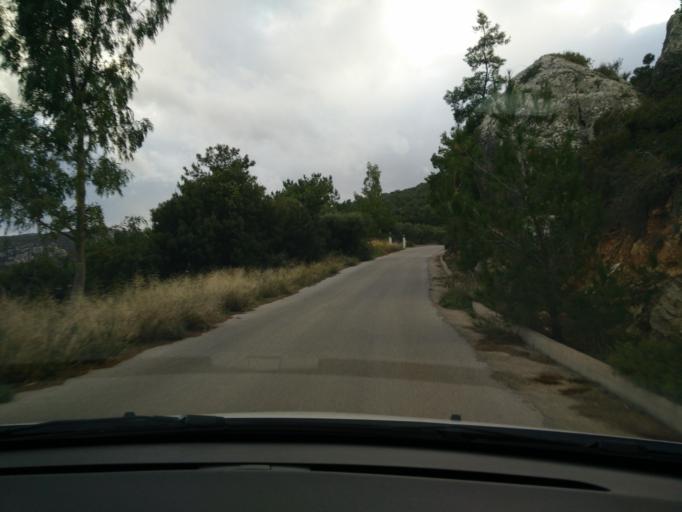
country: GR
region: Crete
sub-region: Nomos Lasithiou
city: Kritsa
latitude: 35.1027
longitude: 25.6938
